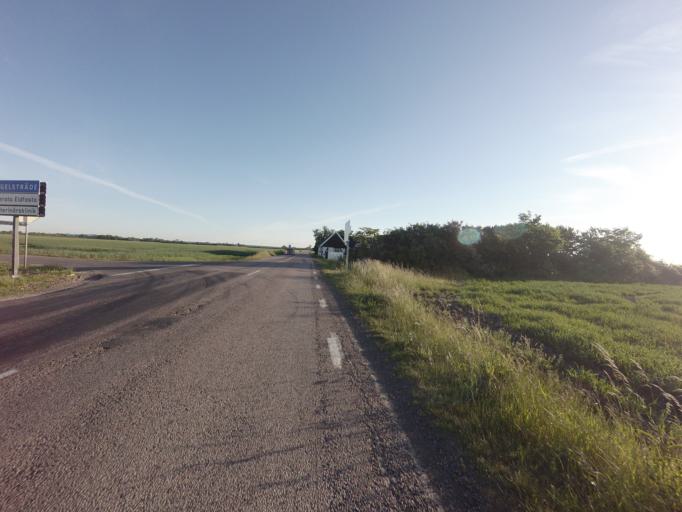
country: SE
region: Skane
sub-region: Helsingborg
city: Odakra
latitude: 56.1831
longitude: 12.6763
